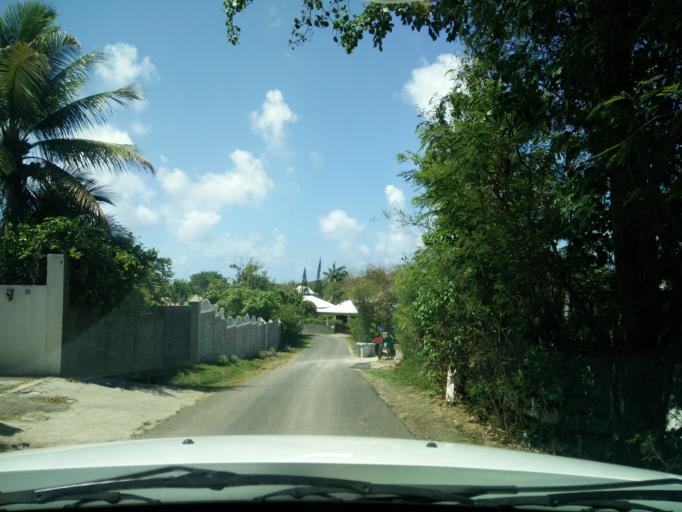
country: GP
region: Guadeloupe
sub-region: Guadeloupe
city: Sainte-Anne
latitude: 16.2447
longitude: -61.3423
